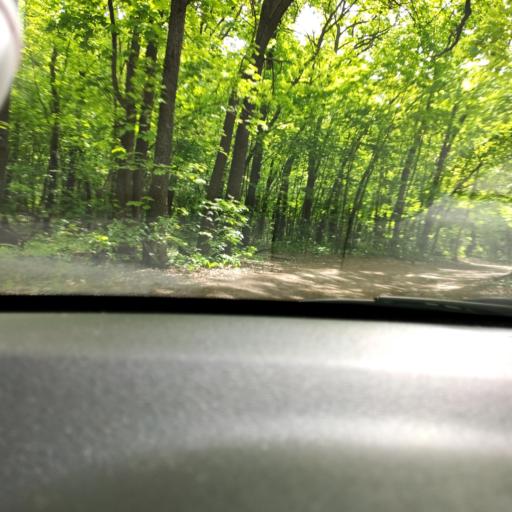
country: RU
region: Samara
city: Samara
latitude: 53.2779
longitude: 50.2229
